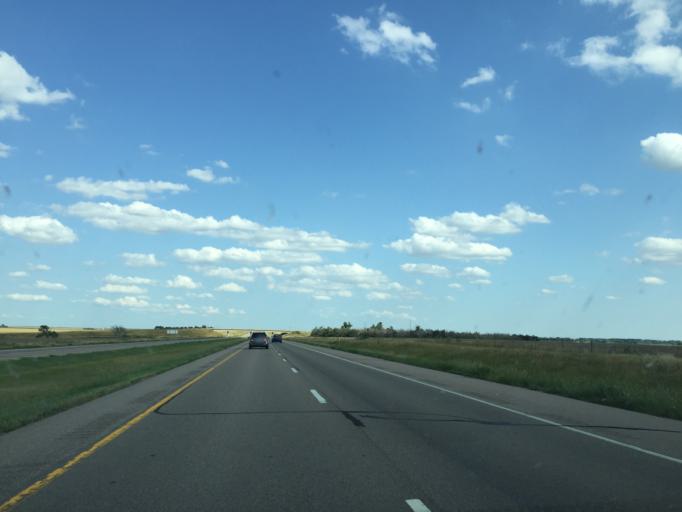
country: US
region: Kansas
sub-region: Gove County
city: Gove
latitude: 39.0517
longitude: -100.2286
